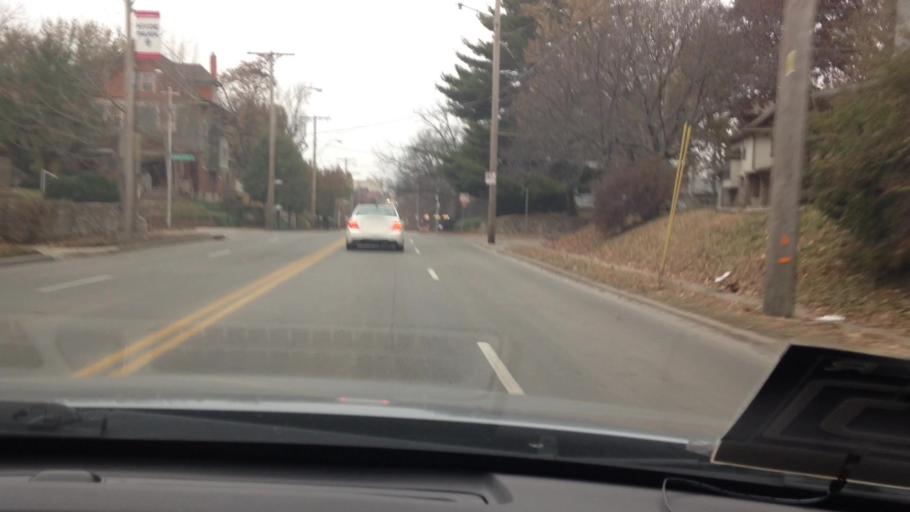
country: US
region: Missouri
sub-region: Jackson County
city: Kansas City
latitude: 39.0562
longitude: -94.5750
